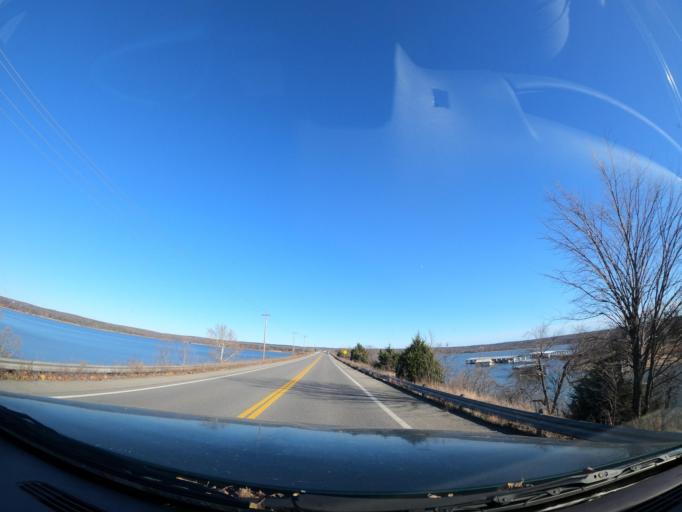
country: US
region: Oklahoma
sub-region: Pittsburg County
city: Longtown
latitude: 35.2392
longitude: -95.5096
